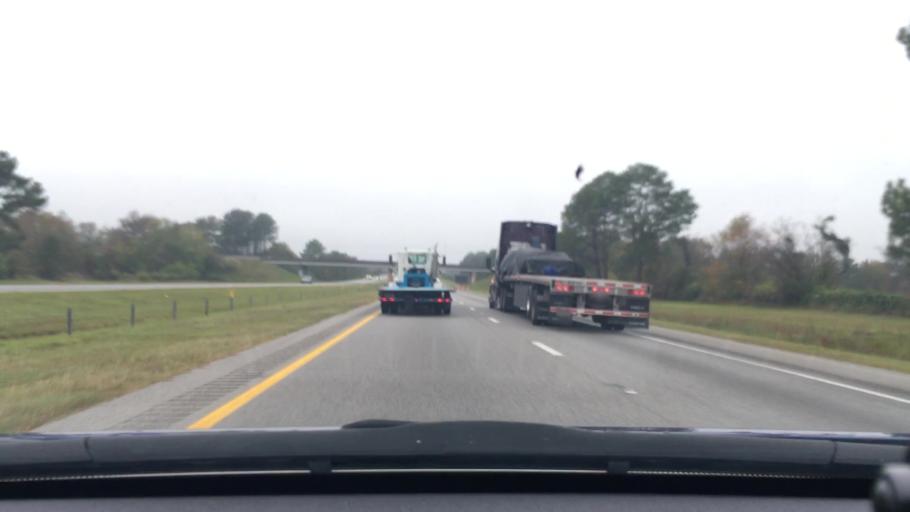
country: US
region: South Carolina
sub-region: Lee County
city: Bishopville
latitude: 34.1898
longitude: -80.2474
